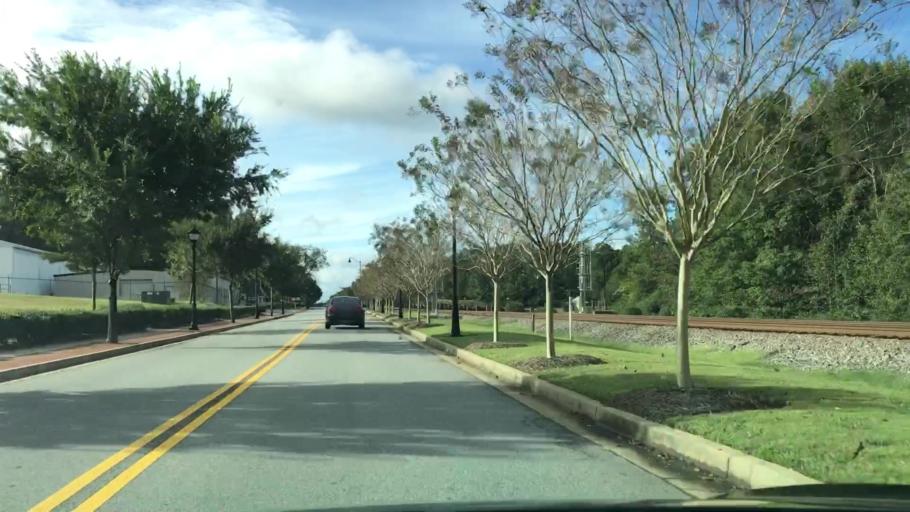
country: US
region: Georgia
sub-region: Gwinnett County
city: Buford
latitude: 34.1325
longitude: -83.9983
